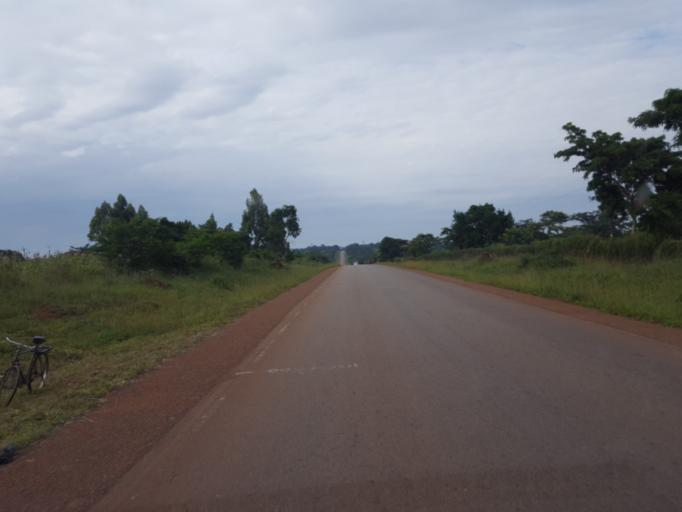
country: UG
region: Central Region
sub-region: Kyankwanzi District
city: Kyankwanzi
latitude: 1.1879
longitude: 31.5640
